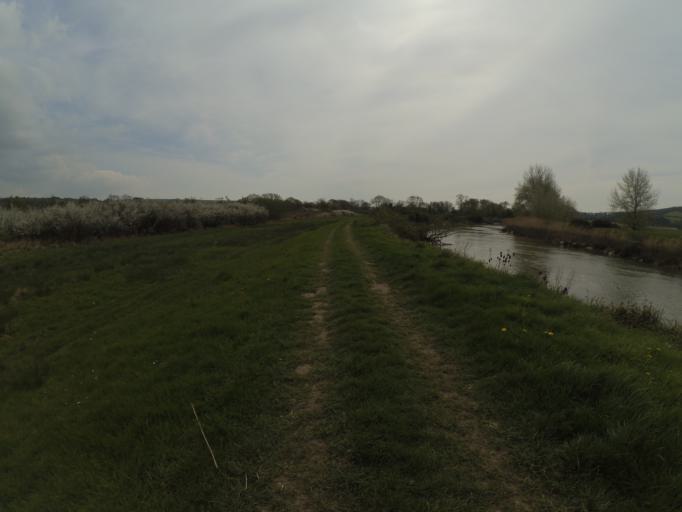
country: GB
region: England
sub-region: West Sussex
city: Arundel
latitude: 50.8813
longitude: -0.5394
